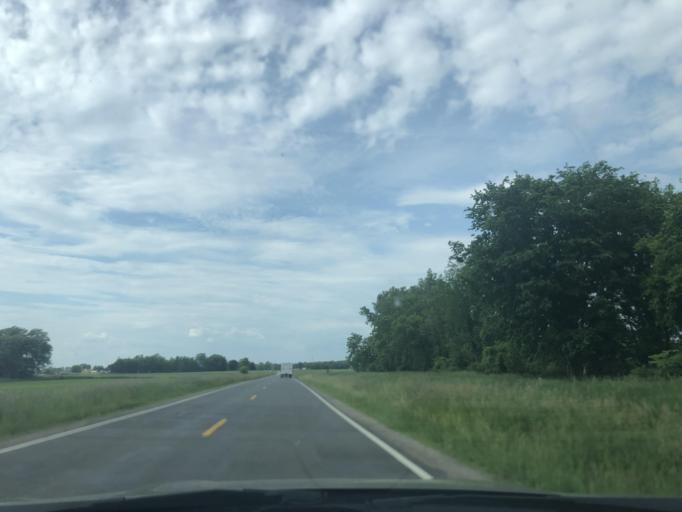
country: US
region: Michigan
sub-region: Clinton County
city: Saint Johns
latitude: 42.9839
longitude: -84.4838
